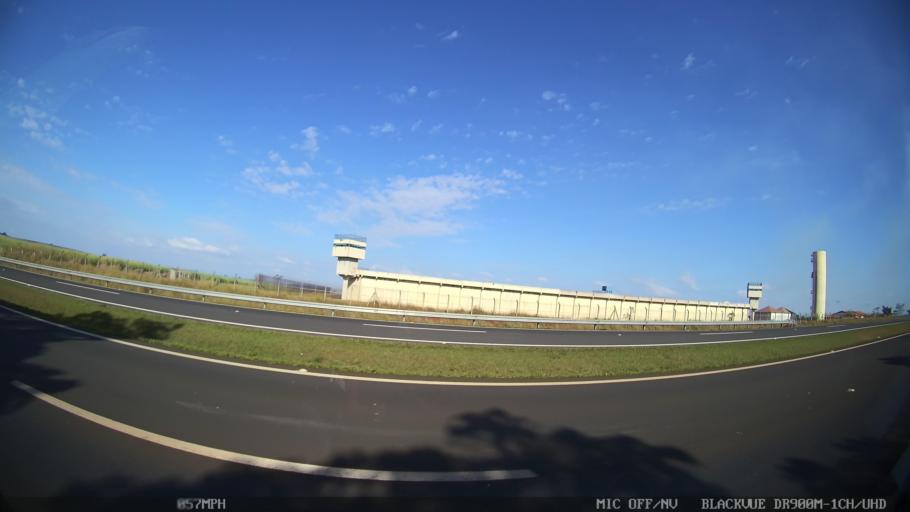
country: BR
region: Sao Paulo
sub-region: Piracicaba
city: Piracicaba
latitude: -22.6763
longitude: -47.5624
